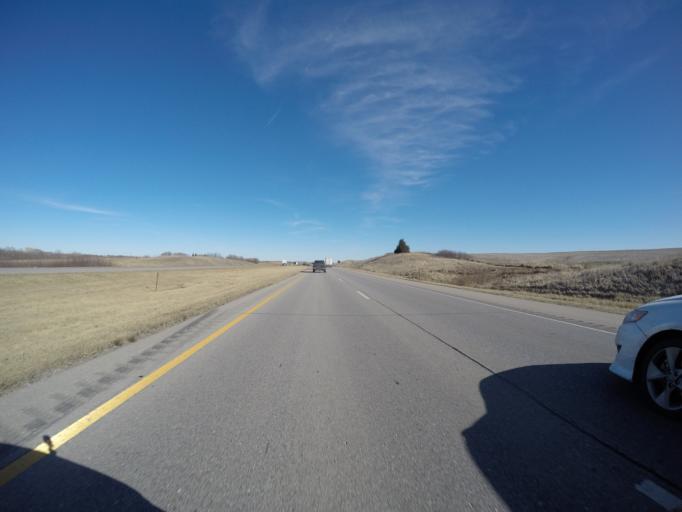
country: US
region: Nebraska
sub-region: Seward County
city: Milford
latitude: 40.8213
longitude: -96.9649
